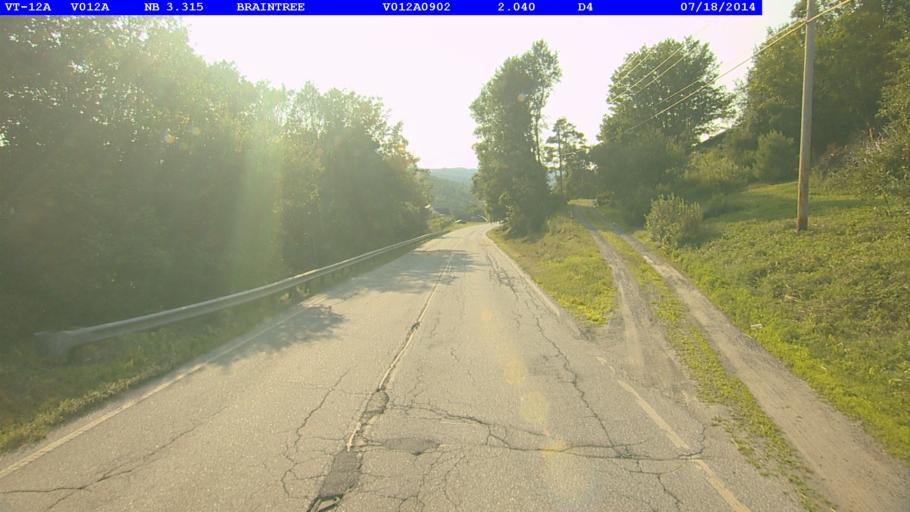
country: US
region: Vermont
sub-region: Orange County
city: Randolph
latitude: 43.9492
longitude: -72.7134
